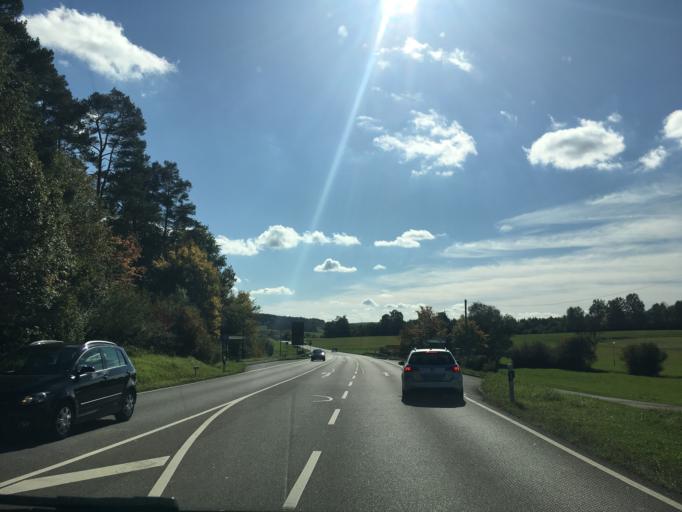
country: DE
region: Baden-Wuerttemberg
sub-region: Karlsruhe Region
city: Althengstett
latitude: 48.7350
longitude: 8.7901
